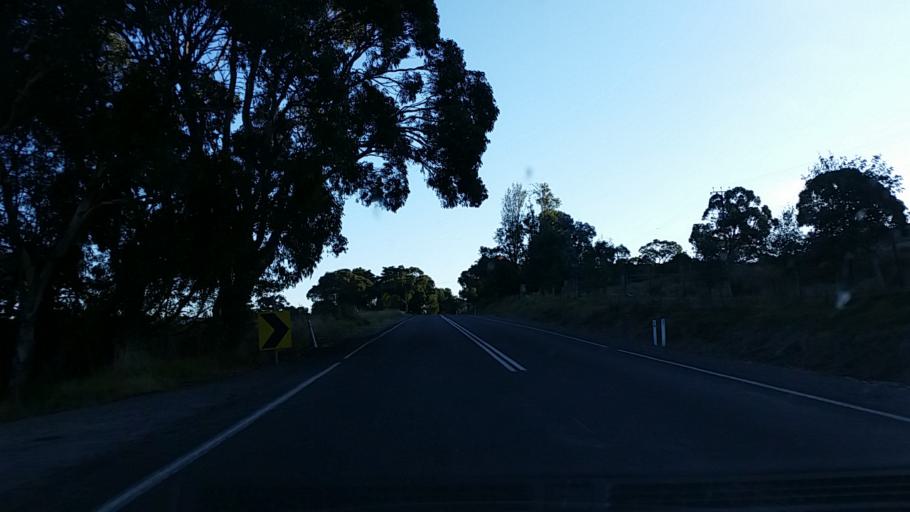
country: AU
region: South Australia
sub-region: Alexandrina
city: Mount Compass
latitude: -35.3471
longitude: 138.6459
